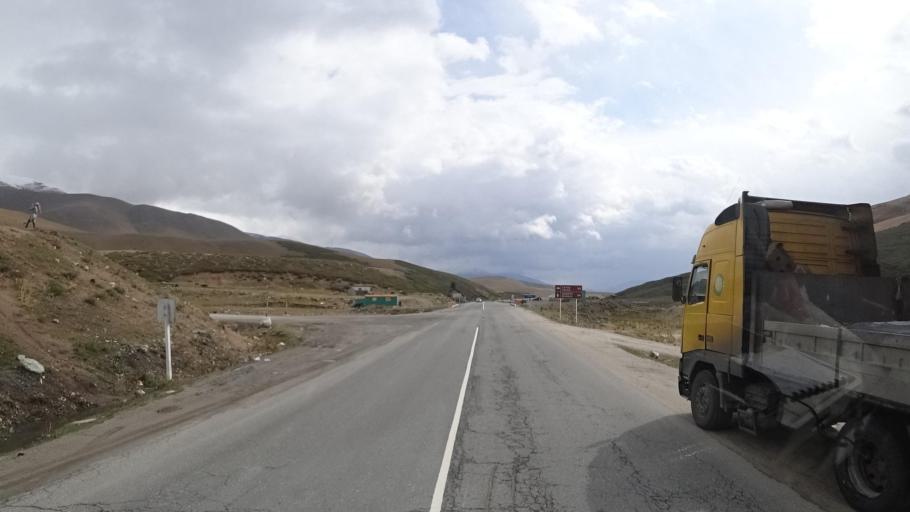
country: KG
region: Jalal-Abad
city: Uch-Terek
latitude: 42.2074
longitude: 73.2507
